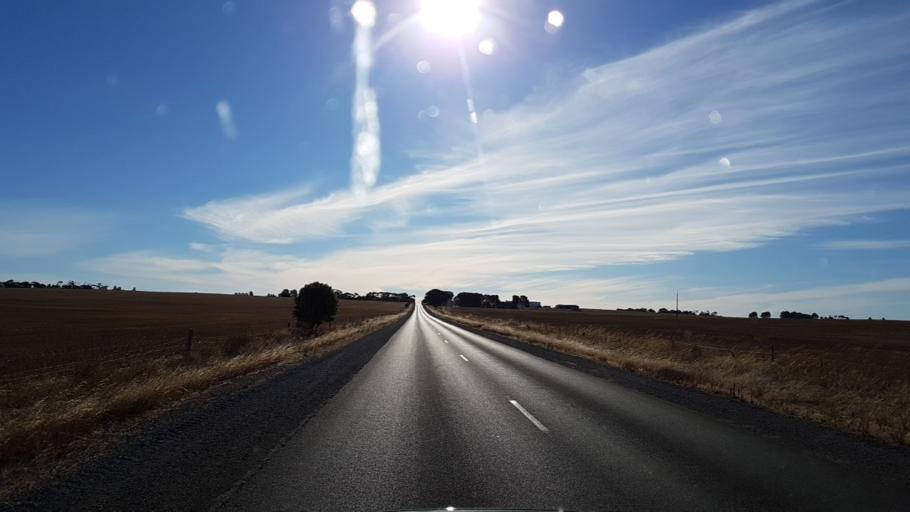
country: AU
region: South Australia
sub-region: Yorke Peninsula
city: Honiton
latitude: -34.9850
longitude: 137.3222
